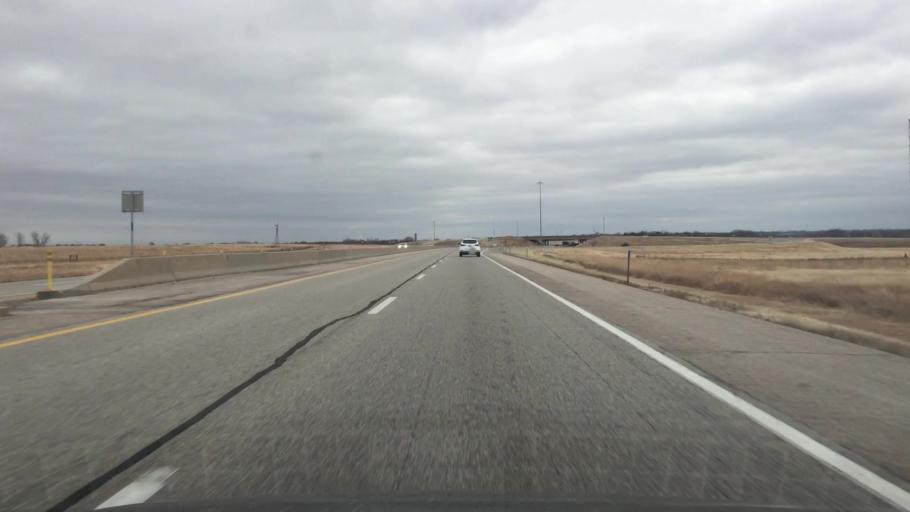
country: US
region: Kansas
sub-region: Butler County
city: El Dorado
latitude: 37.8811
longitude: -96.8426
